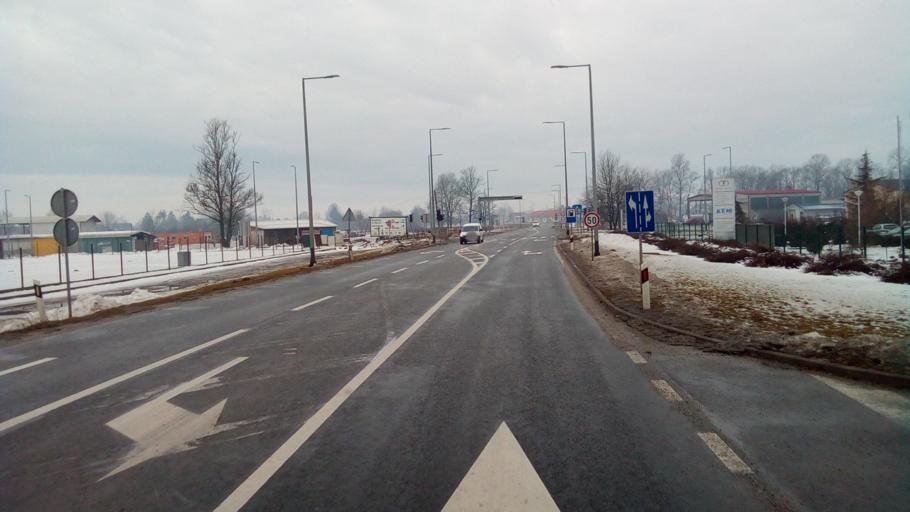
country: HR
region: Zagrebacka
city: Lupoglav
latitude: 45.7010
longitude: 16.4049
